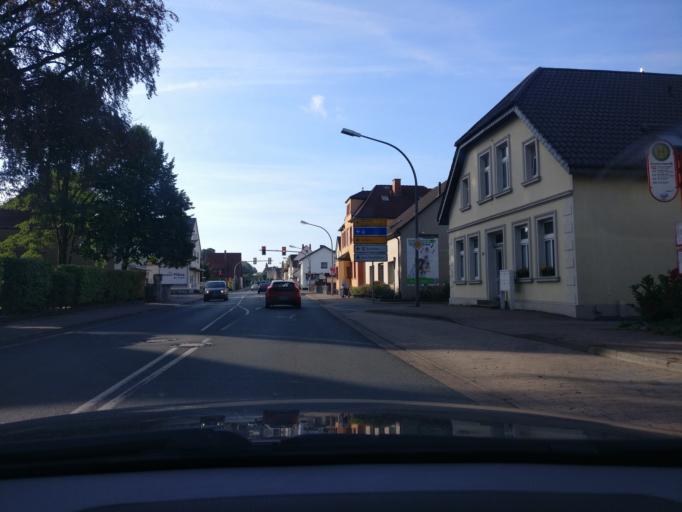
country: DE
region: Lower Saxony
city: Melle
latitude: 52.1983
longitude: 8.3346
